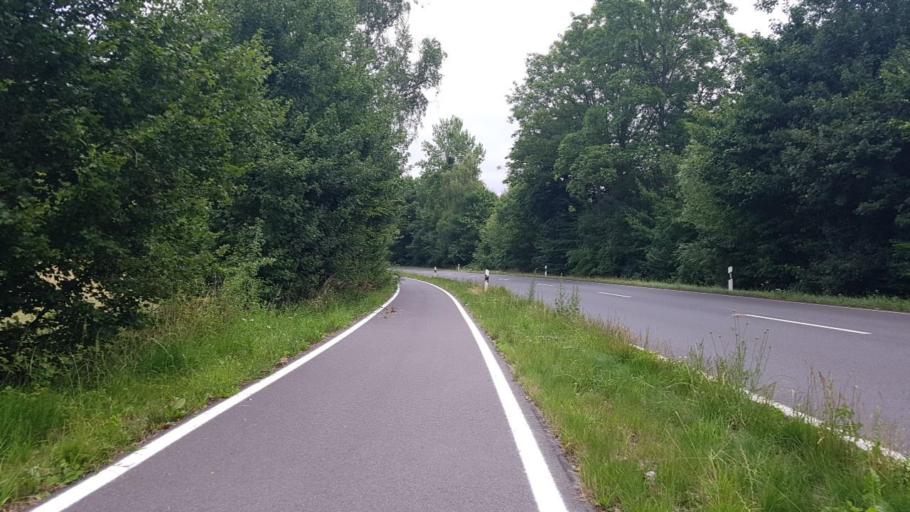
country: DE
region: North Rhine-Westphalia
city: Stolberg
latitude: 50.7847
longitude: 6.1876
